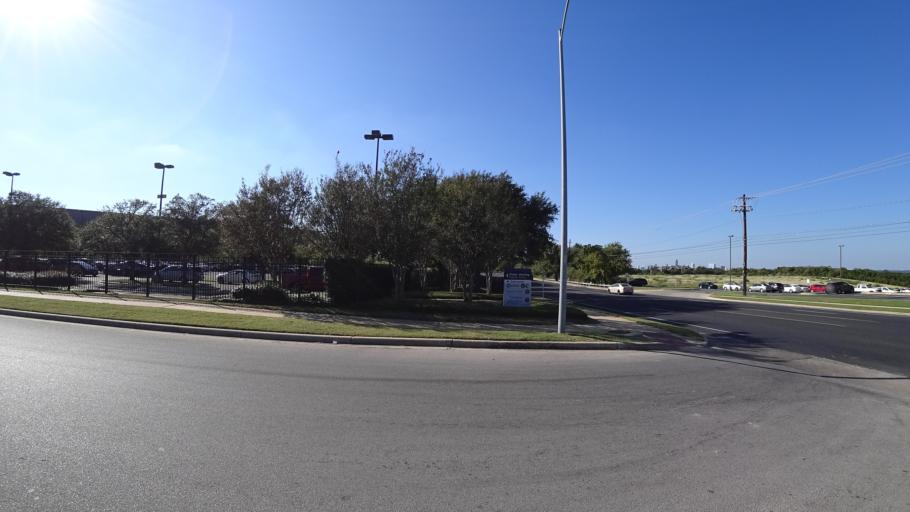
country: US
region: Texas
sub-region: Travis County
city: Austin
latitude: 30.2190
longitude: -97.7187
